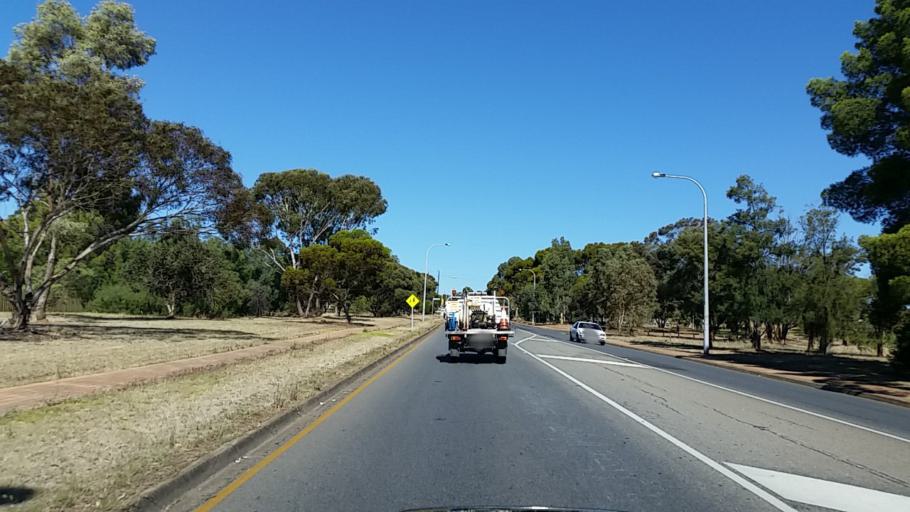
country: AU
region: South Australia
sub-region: Salisbury
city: Elizabeth
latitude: -34.7074
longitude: 138.6955
